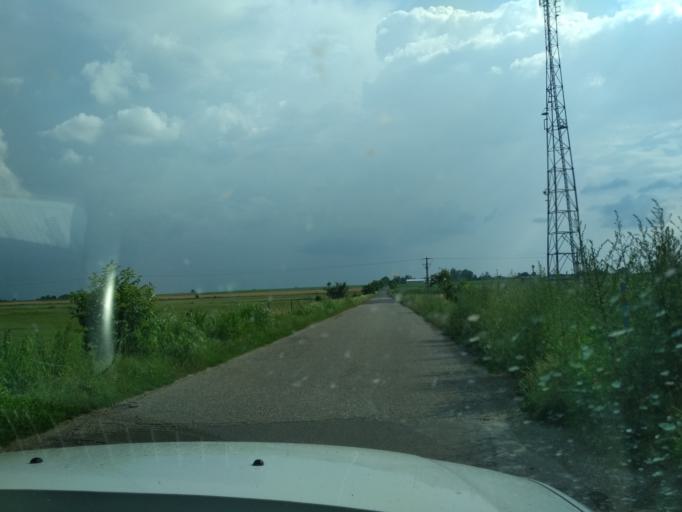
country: HU
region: Pest
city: Tapioszentmarton
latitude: 47.3361
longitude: 19.7412
